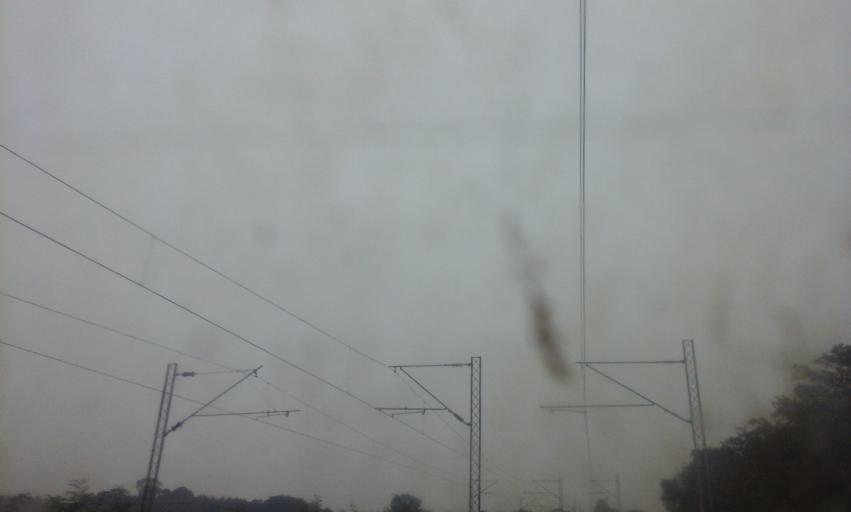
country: RS
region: Central Serbia
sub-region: Pomoravski Okrug
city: Paracin
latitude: 43.8798
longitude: 21.3879
